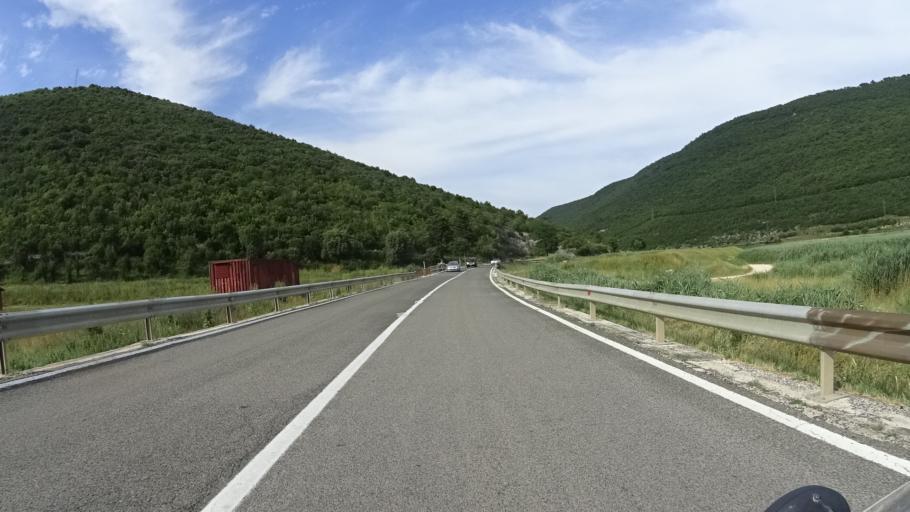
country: HR
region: Istarska
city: Rasa
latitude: 45.0631
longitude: 14.0641
